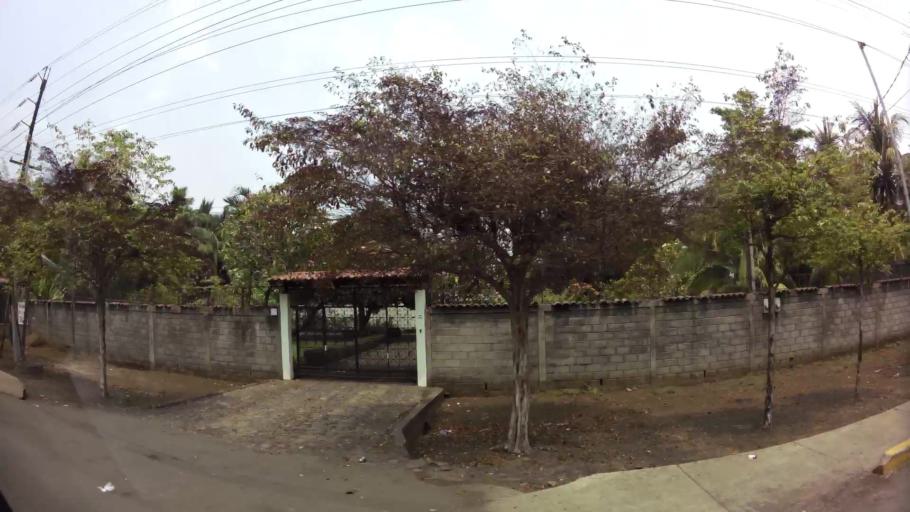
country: NI
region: Chinandega
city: Chinandega
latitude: 12.6274
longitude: -87.1186
